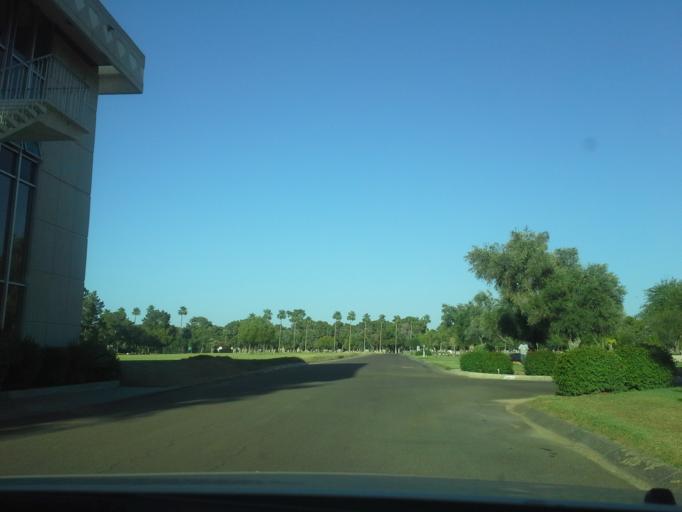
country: US
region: Arizona
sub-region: Maricopa County
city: Phoenix
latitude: 33.4546
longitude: -112.1160
